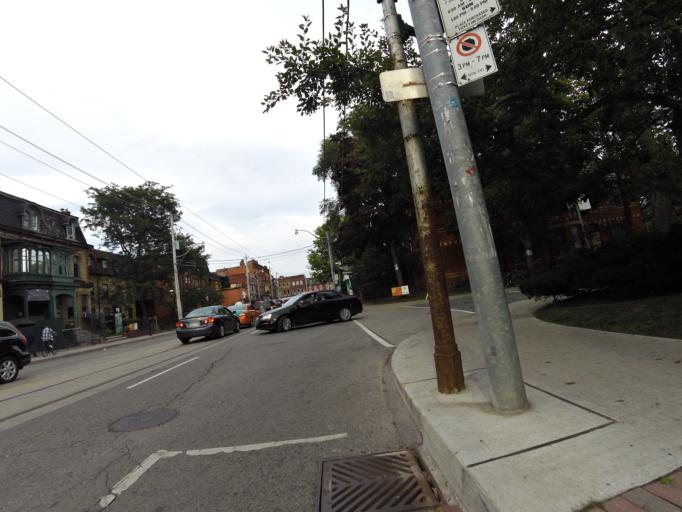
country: CA
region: Ontario
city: Toronto
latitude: 43.6639
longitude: -79.3695
